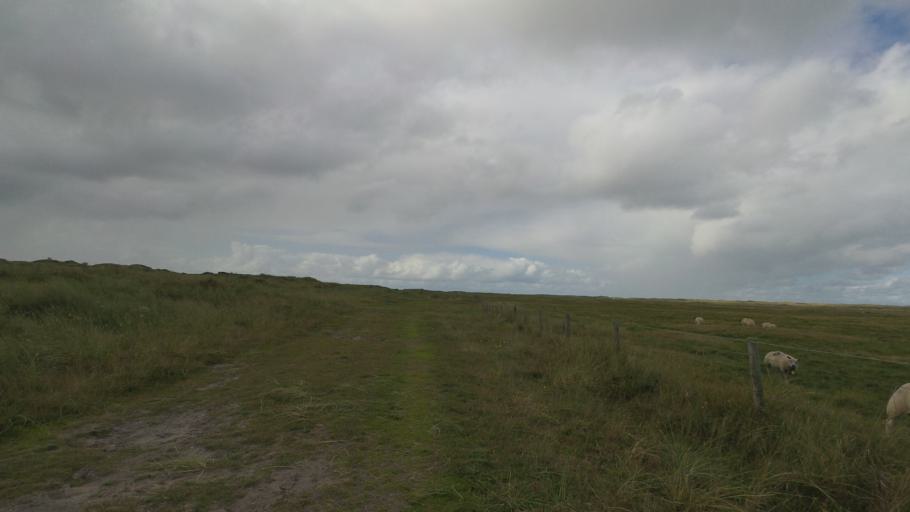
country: NL
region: Friesland
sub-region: Gemeente Ameland
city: Nes
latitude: 53.4515
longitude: 5.8525
